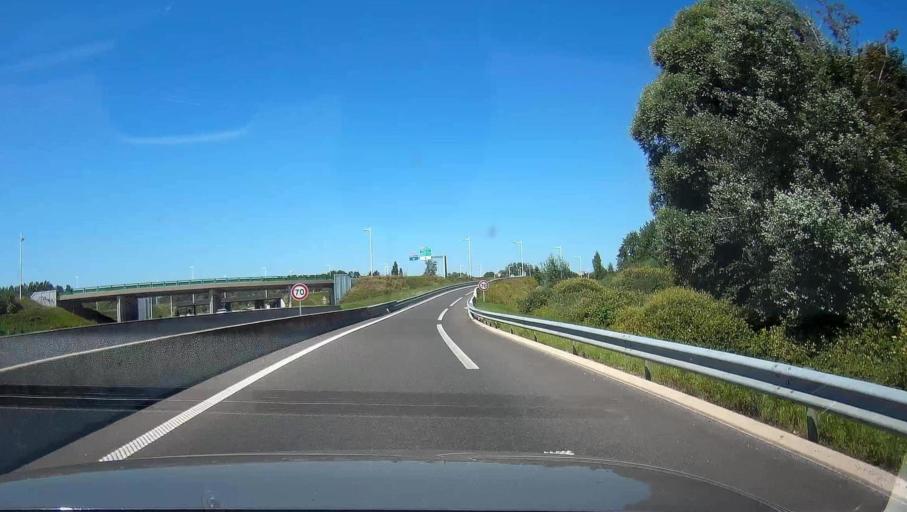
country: FR
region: Champagne-Ardenne
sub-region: Departement de la Marne
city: Cormontreuil
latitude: 49.2221
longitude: 4.0679
